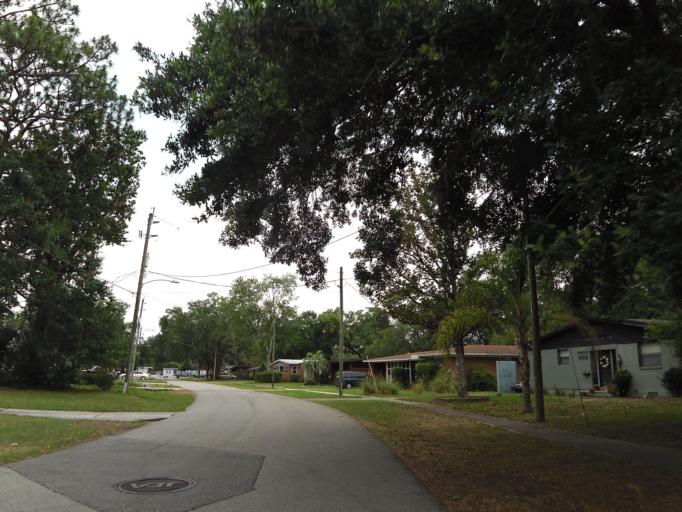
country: US
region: Florida
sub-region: Duval County
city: Jacksonville
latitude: 30.2625
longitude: -81.6360
